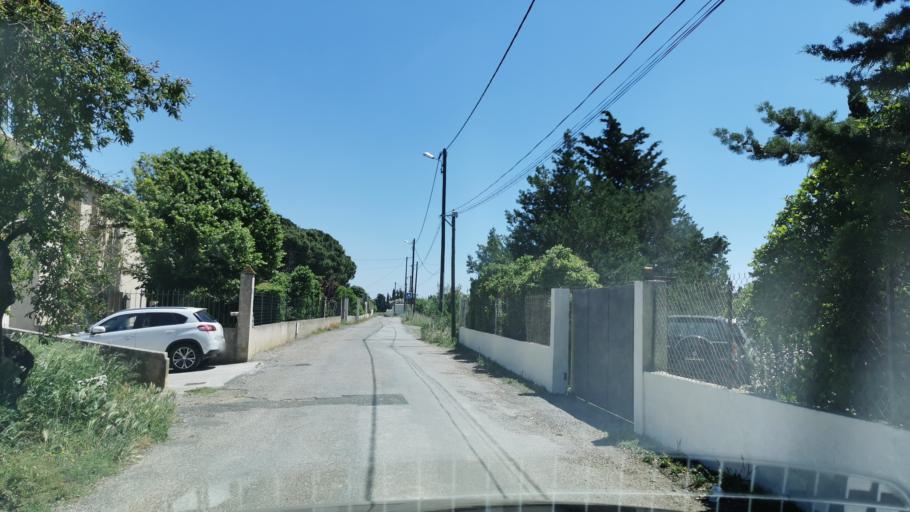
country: FR
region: Languedoc-Roussillon
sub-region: Departement de l'Aude
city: Saint-Marcel-sur-Aude
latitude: 43.2645
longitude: 2.9508
